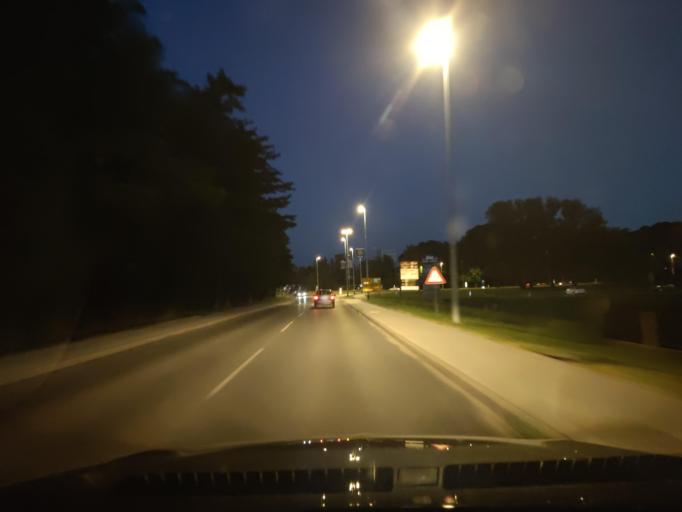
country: HR
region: Medimurska
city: Cakovec
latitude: 46.3928
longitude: 16.4328
